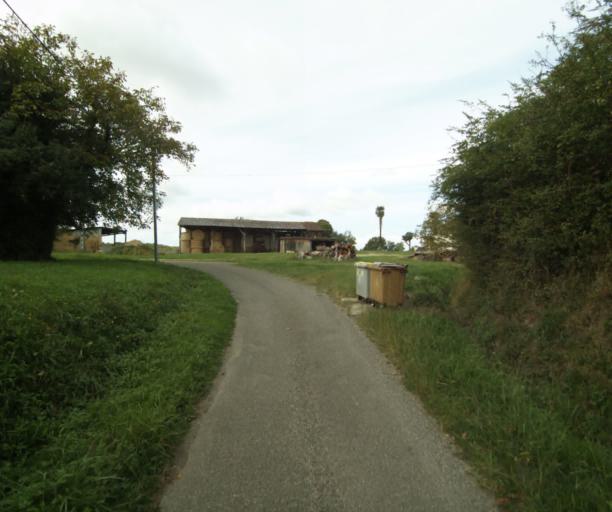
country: FR
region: Midi-Pyrenees
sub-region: Departement du Gers
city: Eauze
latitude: 43.8406
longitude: 0.1159
